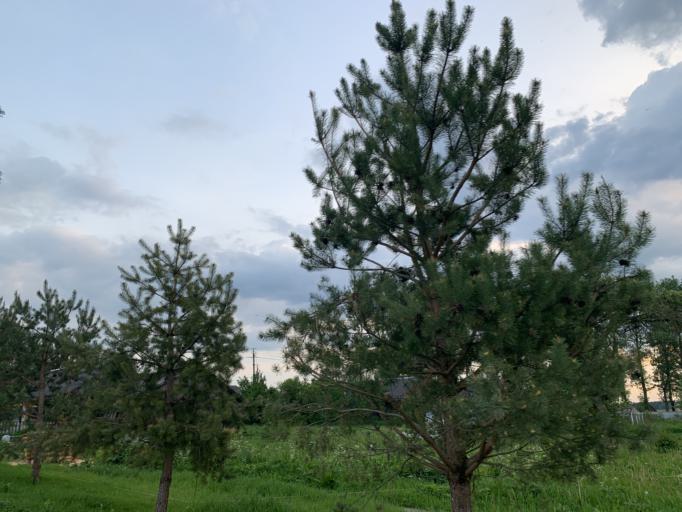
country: BY
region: Minsk
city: Tsimkavichy
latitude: 53.1265
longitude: 26.8829
